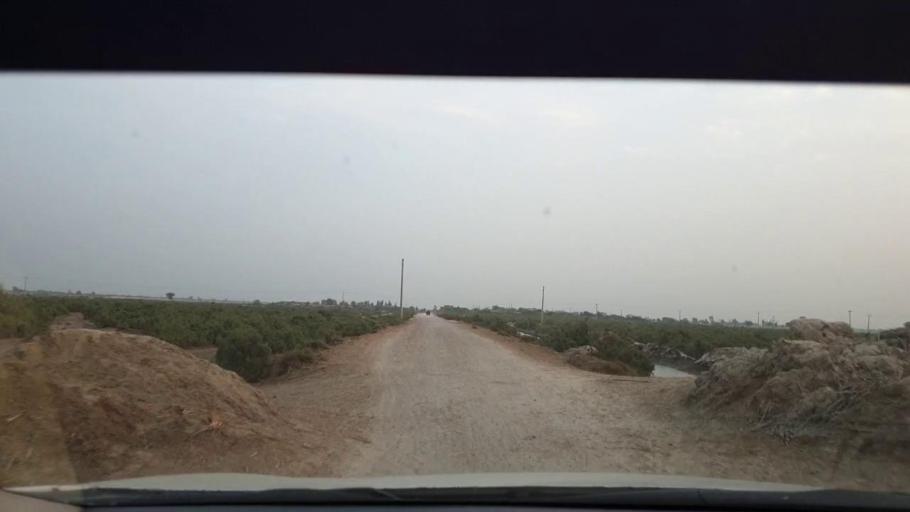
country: PK
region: Sindh
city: Berani
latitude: 25.8830
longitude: 68.7528
